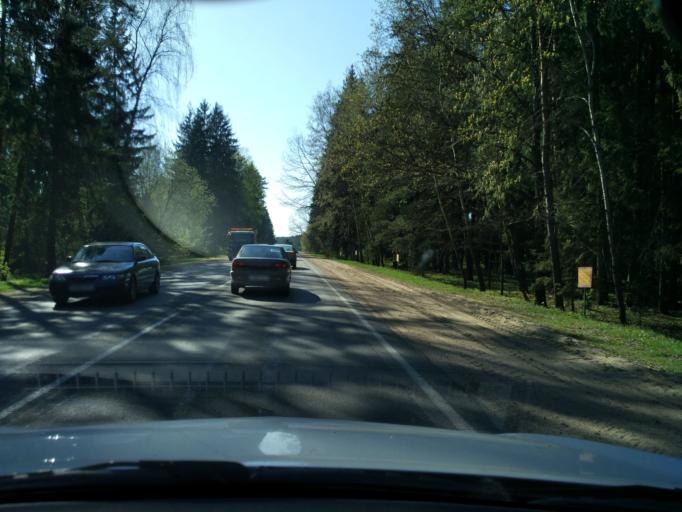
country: BY
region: Minsk
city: Lyeskawka
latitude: 53.9603
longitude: 27.7150
